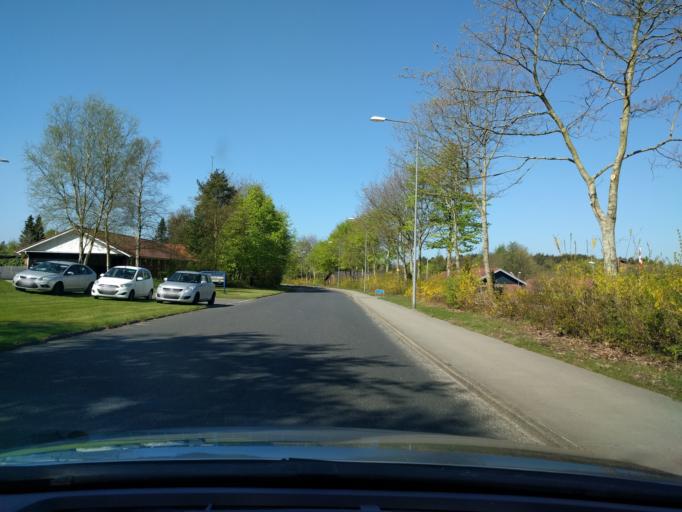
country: DK
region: Central Jutland
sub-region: Herning Kommune
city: Kibaek
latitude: 56.0319
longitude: 8.8472
